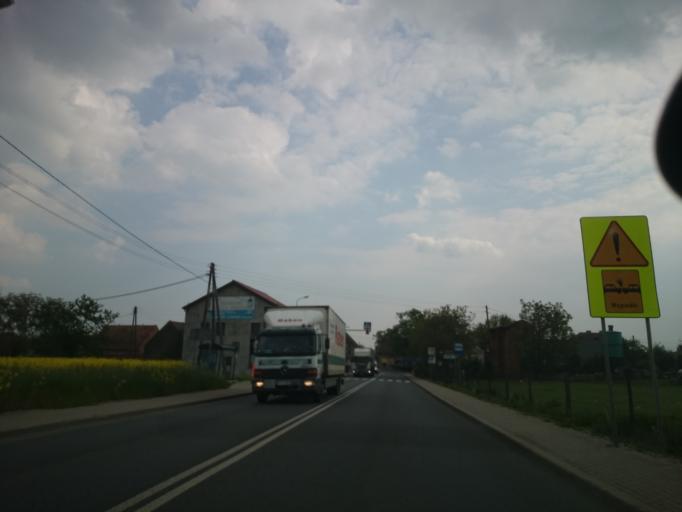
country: PL
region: Lower Silesian Voivodeship
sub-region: Powiat dzierzoniowski
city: Niemcza
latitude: 50.6867
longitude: 16.8201
